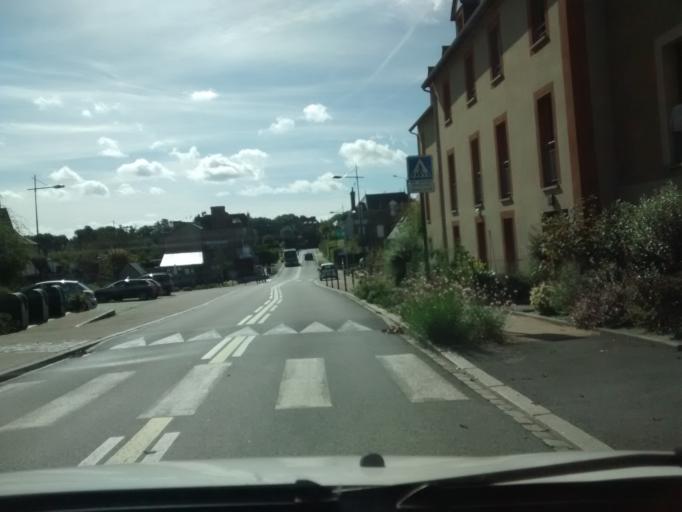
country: FR
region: Brittany
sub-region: Departement d'Ille-et-Vilaine
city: La Richardais
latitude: 48.6057
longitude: -2.0336
